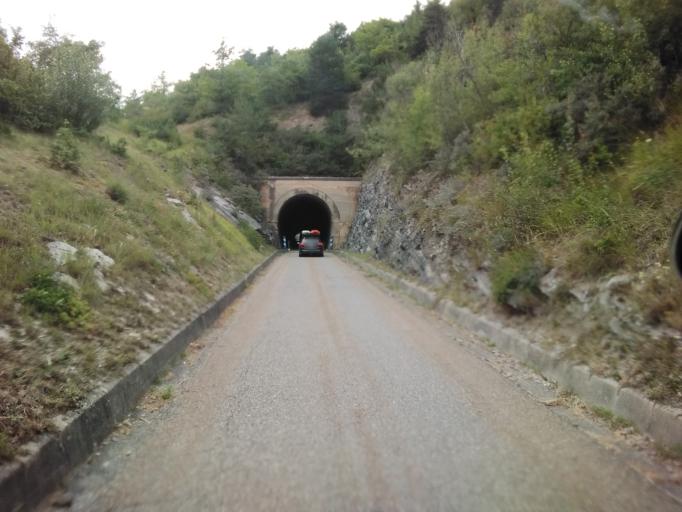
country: FR
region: Provence-Alpes-Cote d'Azur
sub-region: Departement des Alpes-de-Haute-Provence
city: Seyne-les-Alpes
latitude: 44.4576
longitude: 6.3815
